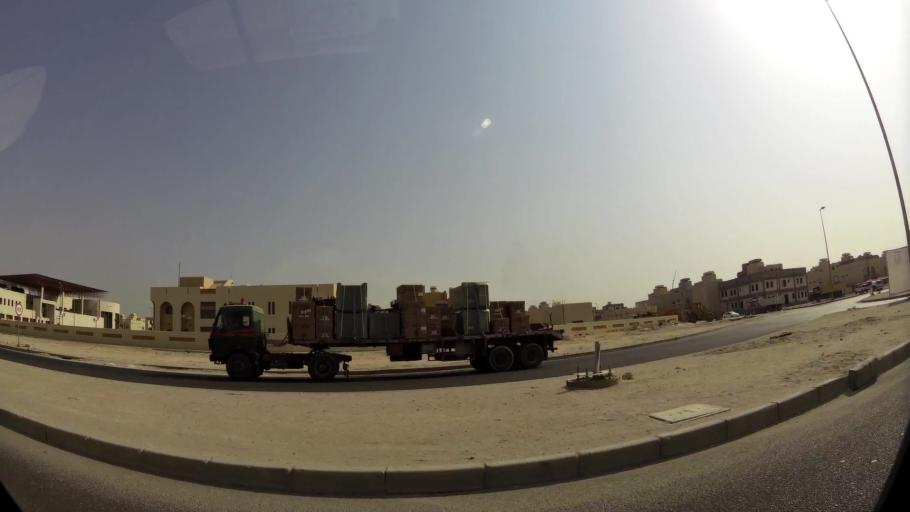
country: KW
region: Muhafazat al Jahra'
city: Al Jahra'
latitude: 29.3494
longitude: 47.7587
